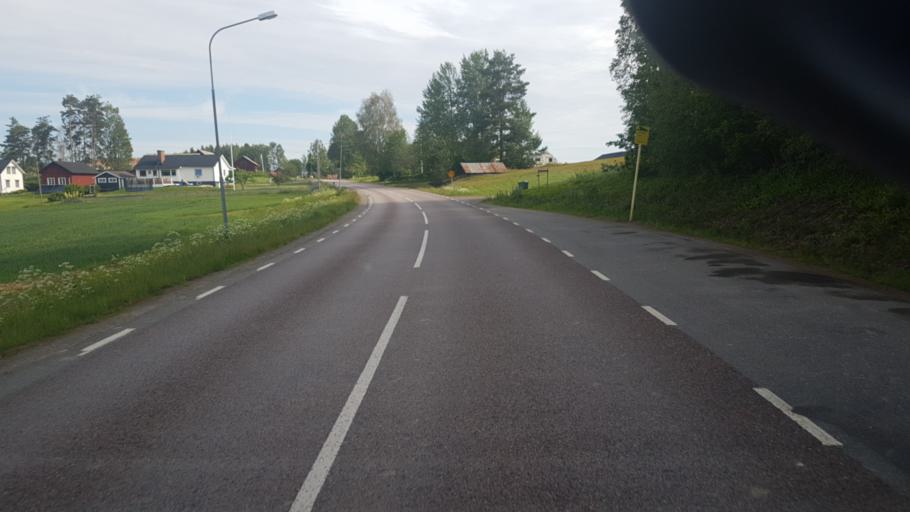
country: SE
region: Vaermland
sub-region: Arvika Kommun
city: Arvika
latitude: 59.7789
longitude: 12.5512
